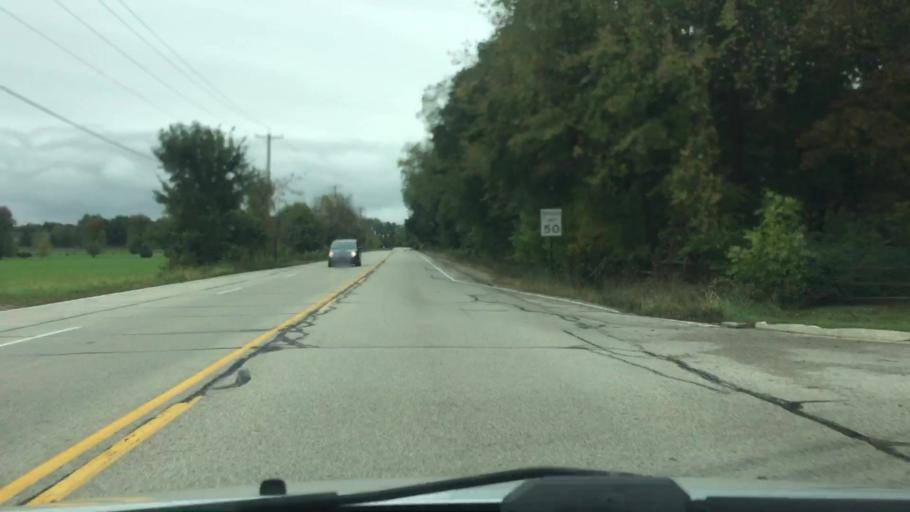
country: US
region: Wisconsin
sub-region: Walworth County
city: Elkhorn
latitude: 42.7747
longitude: -88.5547
